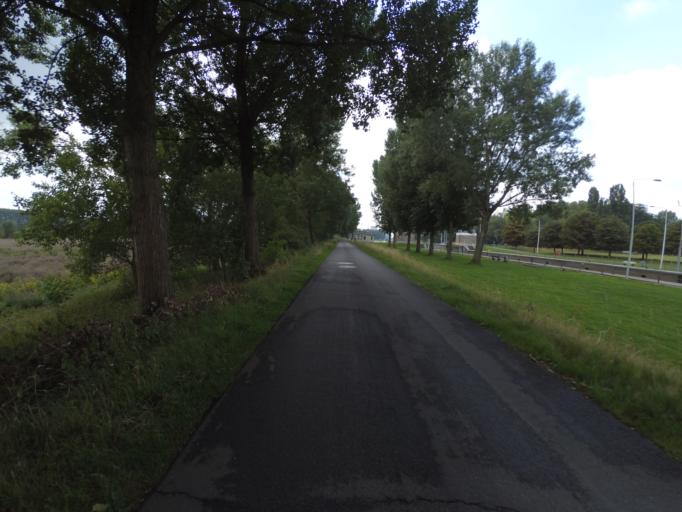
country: NL
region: Limburg
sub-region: Gemeente Maasgouw
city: Maasbracht
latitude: 51.1759
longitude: 5.9247
